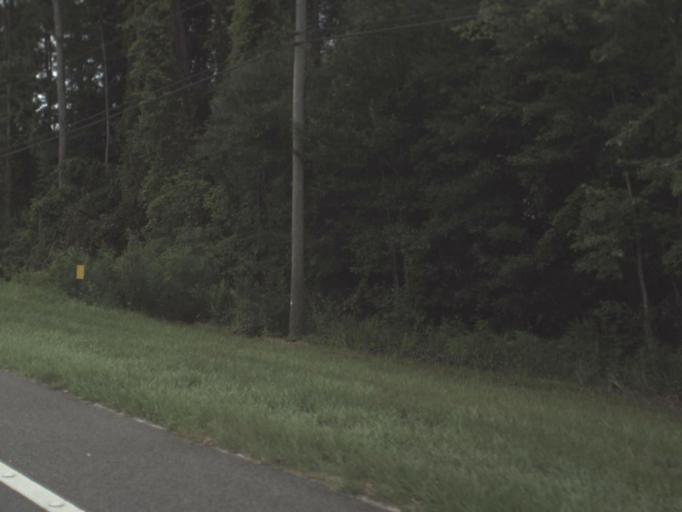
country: US
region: Florida
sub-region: Clay County
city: Keystone Heights
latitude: 29.8305
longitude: -82.0617
